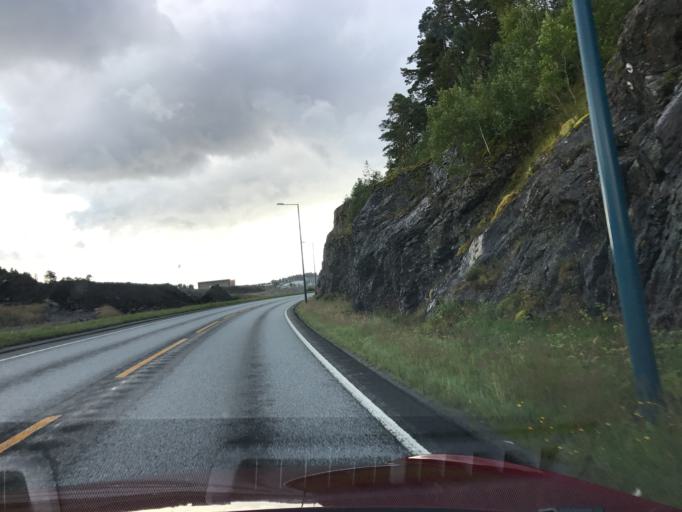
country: NO
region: Hordaland
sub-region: Stord
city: Sagvag
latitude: 59.7609
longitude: 5.4309
